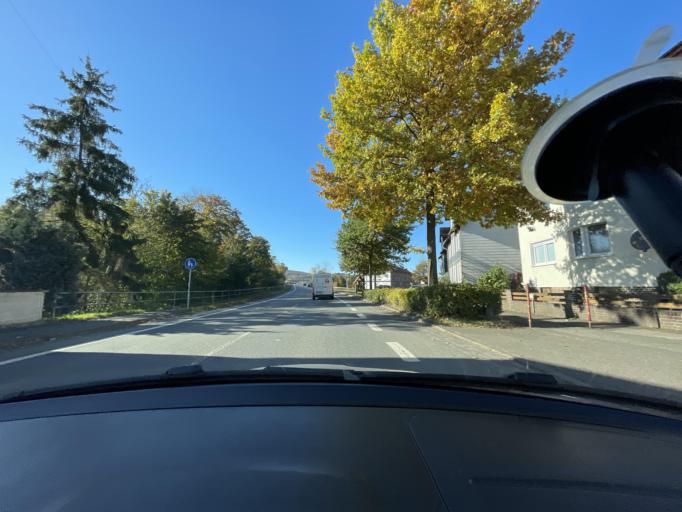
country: DE
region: Lower Saxony
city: Kreiensen
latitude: 51.8580
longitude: 9.9583
